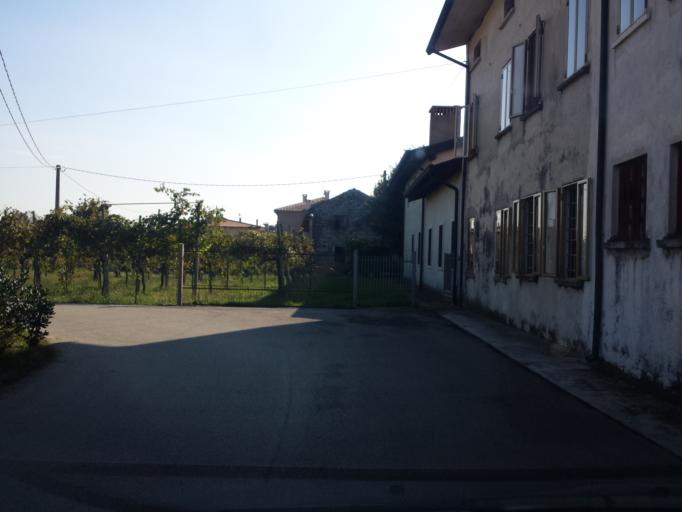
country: IT
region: Veneto
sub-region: Provincia di Vicenza
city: Sandrigo
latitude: 45.6517
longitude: 11.6007
